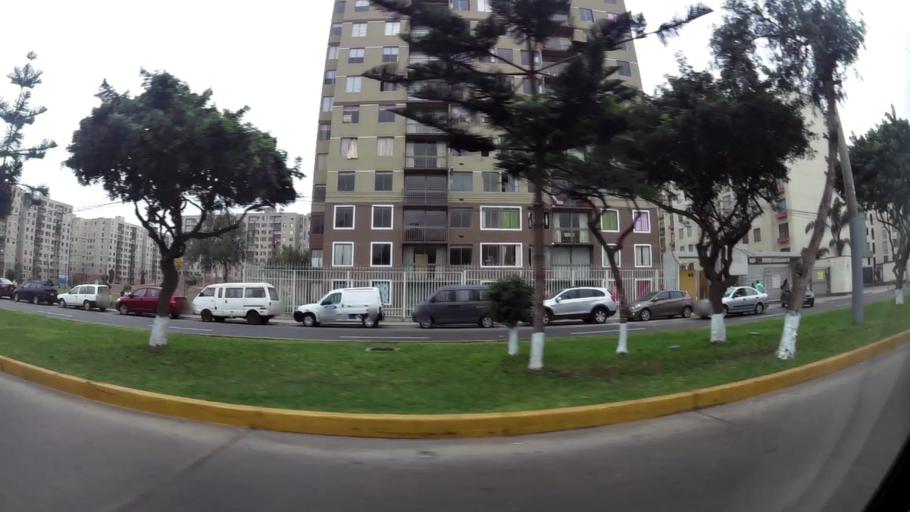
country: PE
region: Callao
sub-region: Callao
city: Callao
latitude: -12.0832
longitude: -77.0894
